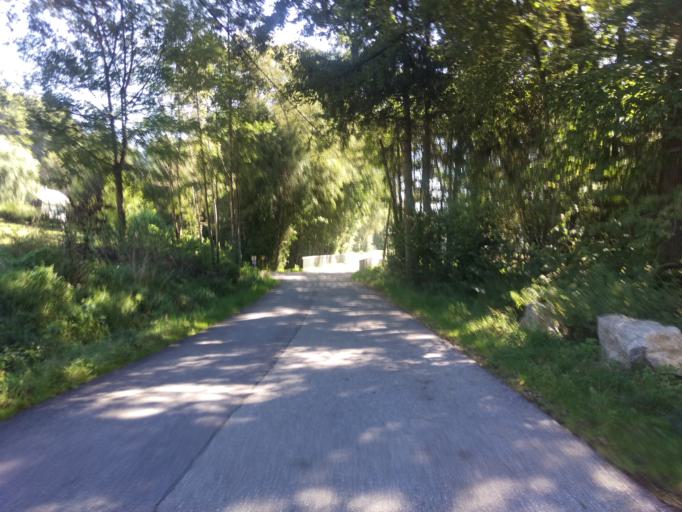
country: AT
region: Styria
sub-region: Politischer Bezirk Graz-Umgebung
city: Hart bei Graz
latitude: 47.0502
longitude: 15.5371
